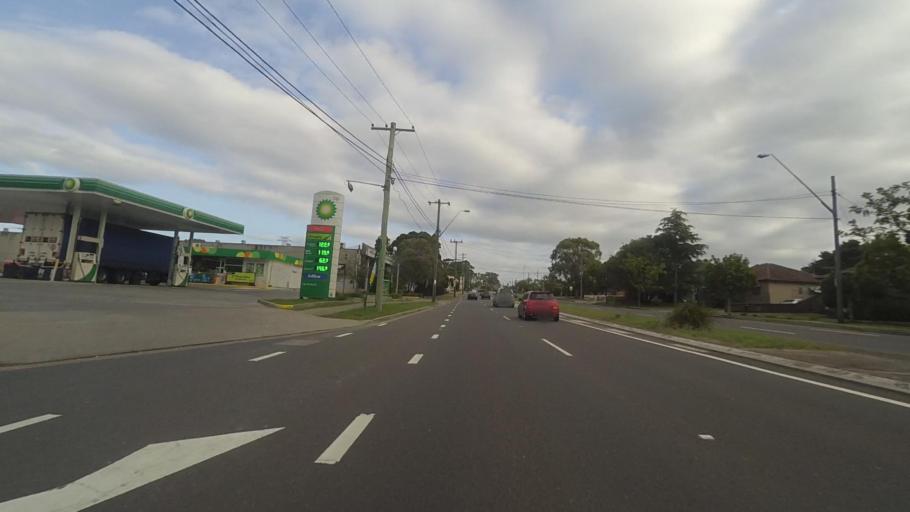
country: AU
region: New South Wales
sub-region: Bankstown
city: Padstow
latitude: -33.9472
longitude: 151.0366
